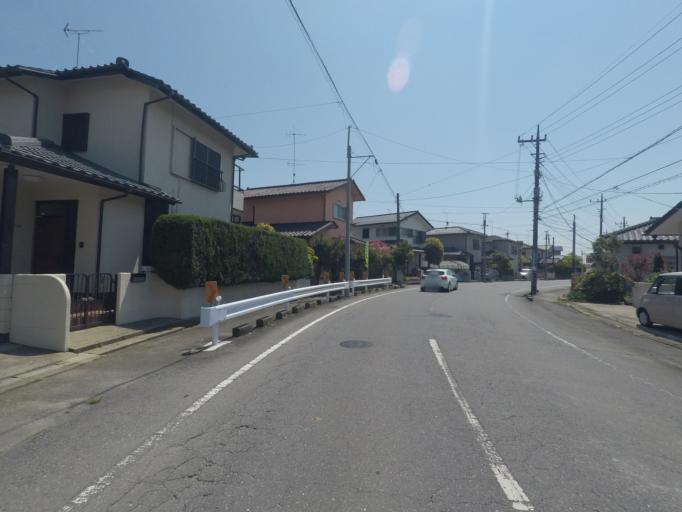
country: JP
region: Ibaraki
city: Ushiku
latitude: 35.9880
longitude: 140.1111
